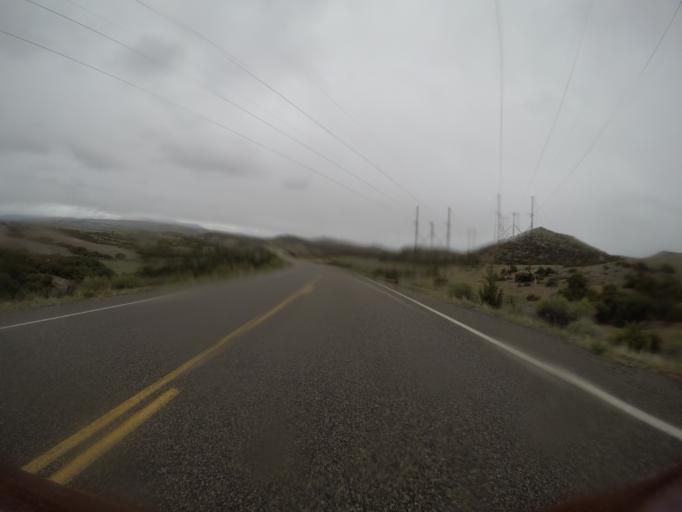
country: US
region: Wyoming
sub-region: Big Horn County
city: Lovell
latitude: 45.0212
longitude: -108.2699
